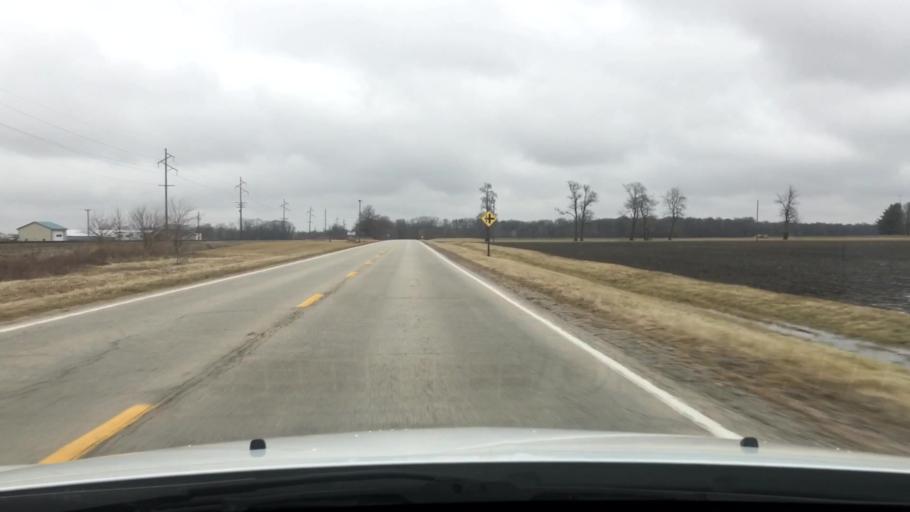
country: US
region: Illinois
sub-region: Iroquois County
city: Sheldon
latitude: 40.8074
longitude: -87.5749
